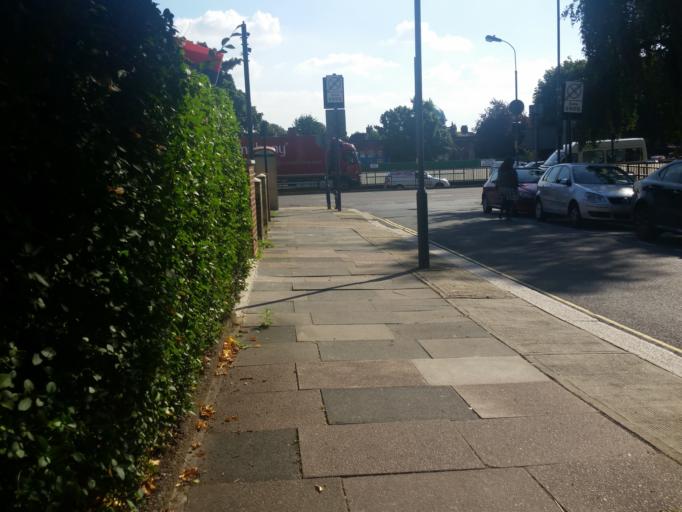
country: GB
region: England
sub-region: Greater London
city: Hammersmith
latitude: 51.5147
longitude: -0.2423
